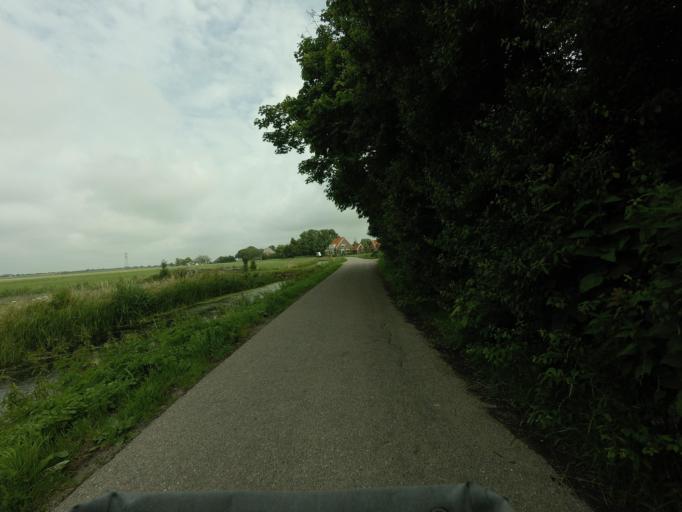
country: NL
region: North Holland
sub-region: Gemeente Schagen
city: Schagen
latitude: 52.7940
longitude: 4.8187
